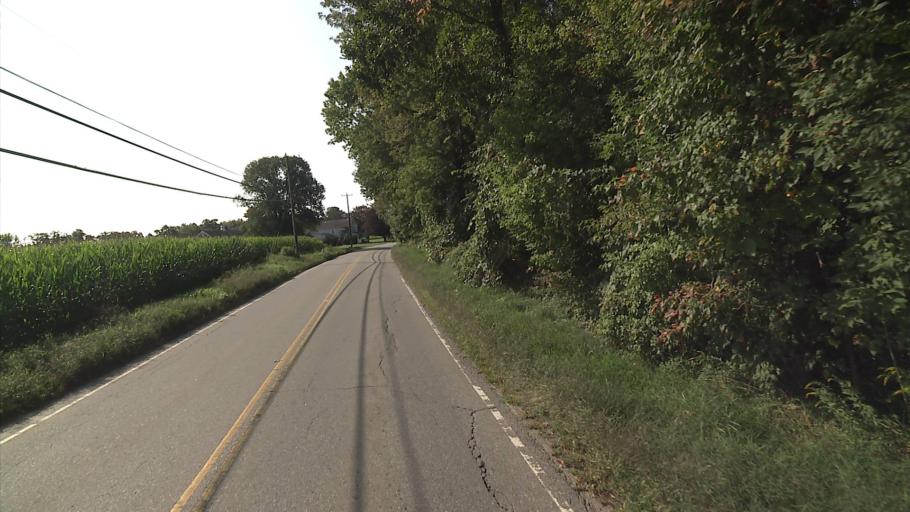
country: US
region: Connecticut
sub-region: Windham County
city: South Windham
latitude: 41.6236
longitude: -72.1974
